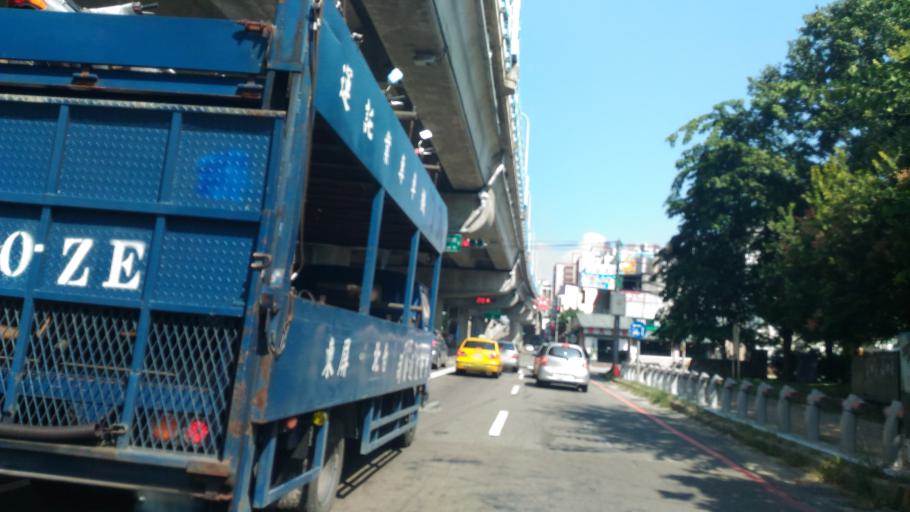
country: TW
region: Taiwan
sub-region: Hsinchu
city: Hsinchu
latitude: 24.8202
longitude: 120.9676
